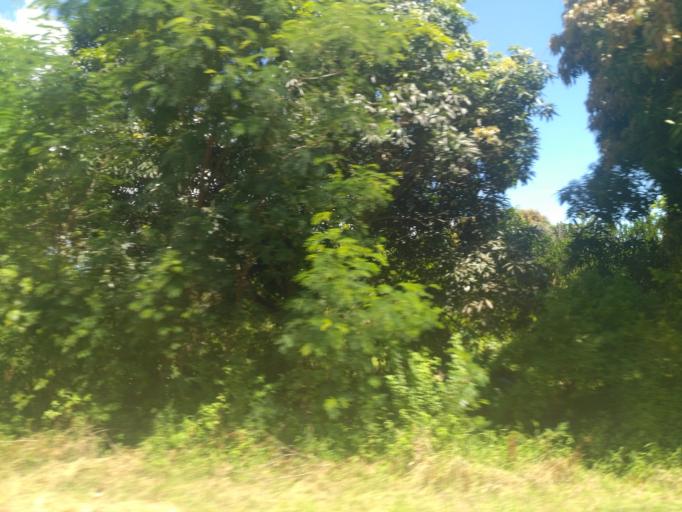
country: TZ
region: Zanzibar North
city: Gamba
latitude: -5.9268
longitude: 39.3446
